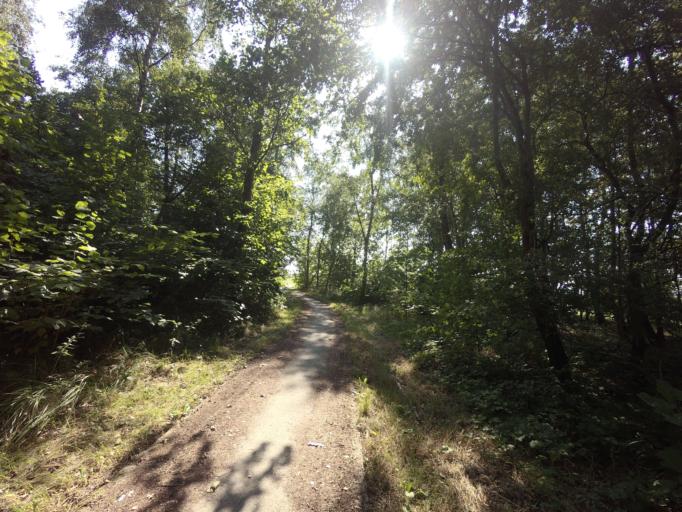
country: NL
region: Groningen
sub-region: Gemeente De Marne
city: Ulrum
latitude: 53.3917
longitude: 6.2659
